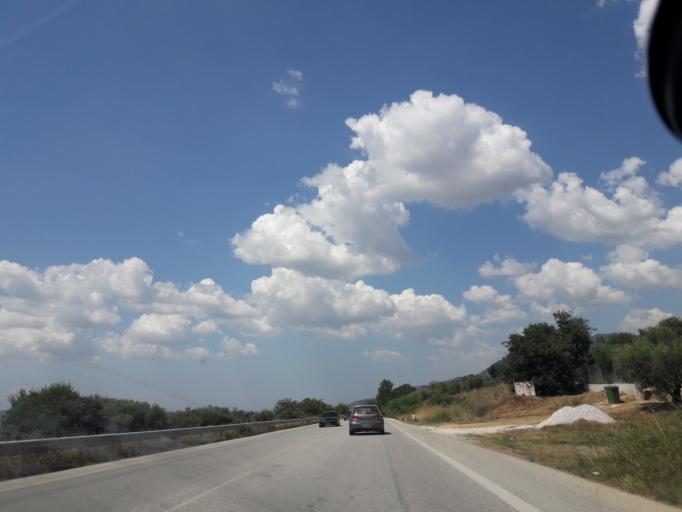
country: GR
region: Central Macedonia
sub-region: Nomos Chalkidikis
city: Galatista
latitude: 40.4614
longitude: 23.2809
